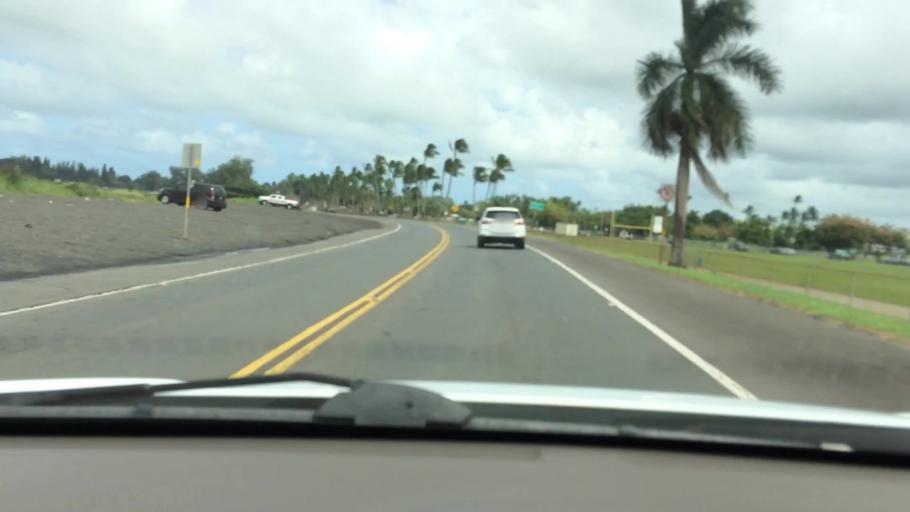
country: US
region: Hawaii
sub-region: Hawaii County
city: Hilo
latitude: 19.7242
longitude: -155.0838
